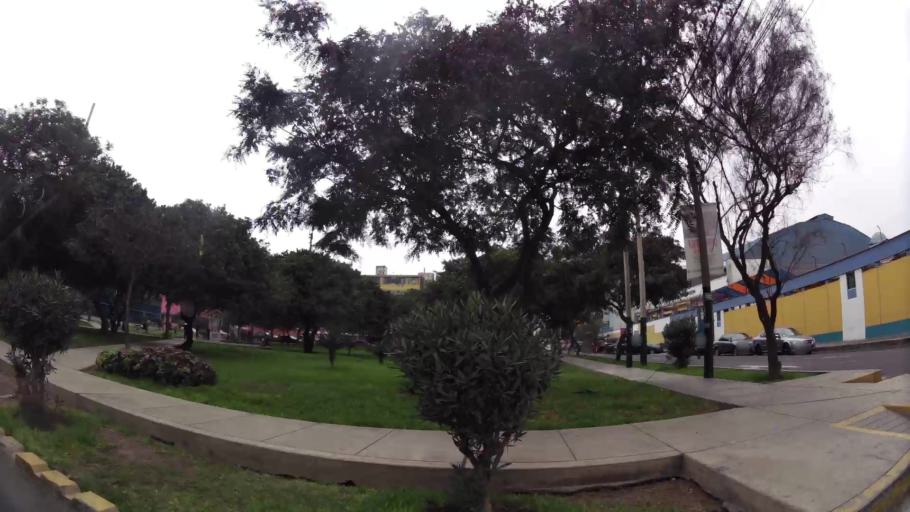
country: PE
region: Lima
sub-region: Lima
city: Surco
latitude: -12.1276
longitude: -76.9995
